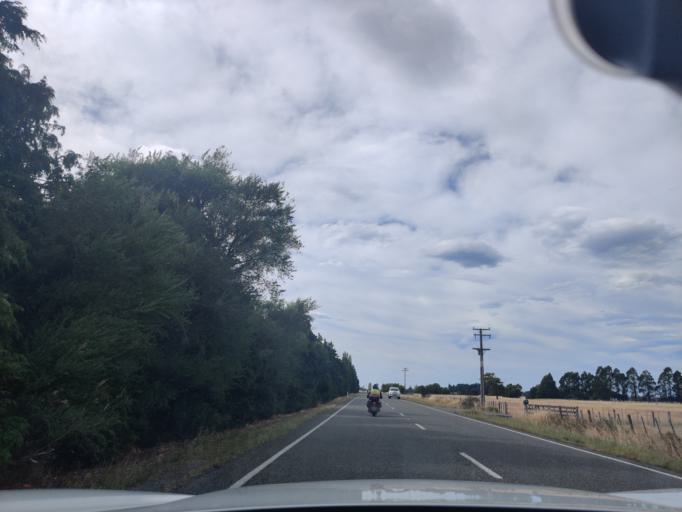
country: NZ
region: Wellington
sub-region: Masterton District
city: Masterton
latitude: -40.8677
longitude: 175.6462
